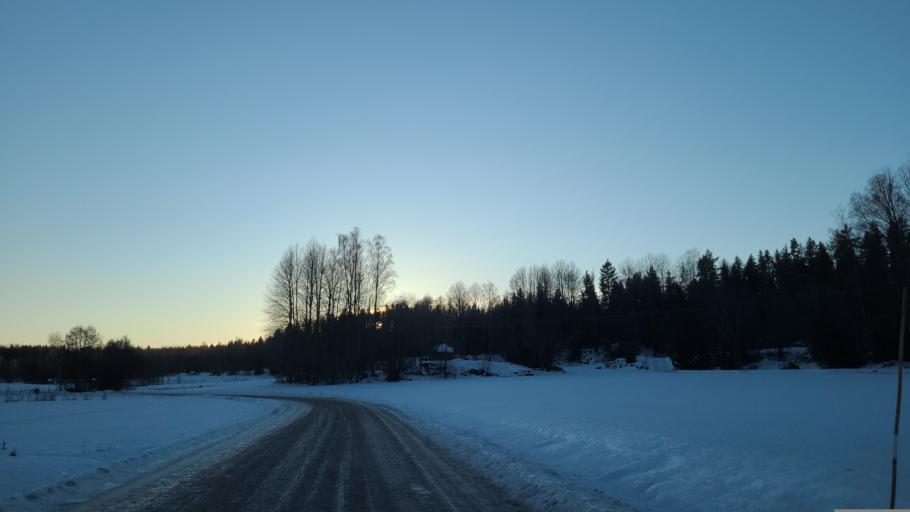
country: SE
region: Gaevleborg
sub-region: Soderhamns Kommun
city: Soderhamn
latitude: 61.2711
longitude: 16.9962
